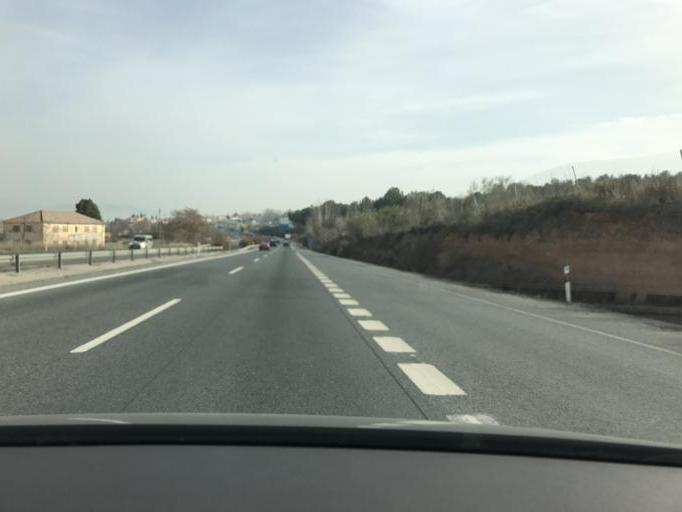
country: ES
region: Andalusia
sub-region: Provincia de Granada
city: Lachar
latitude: 37.1941
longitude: -3.8516
